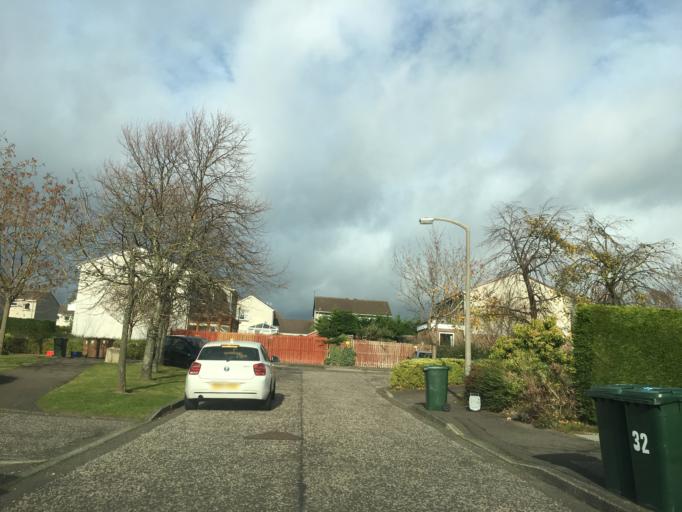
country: GB
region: Scotland
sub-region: Midlothian
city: Loanhead
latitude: 55.9040
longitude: -3.1724
